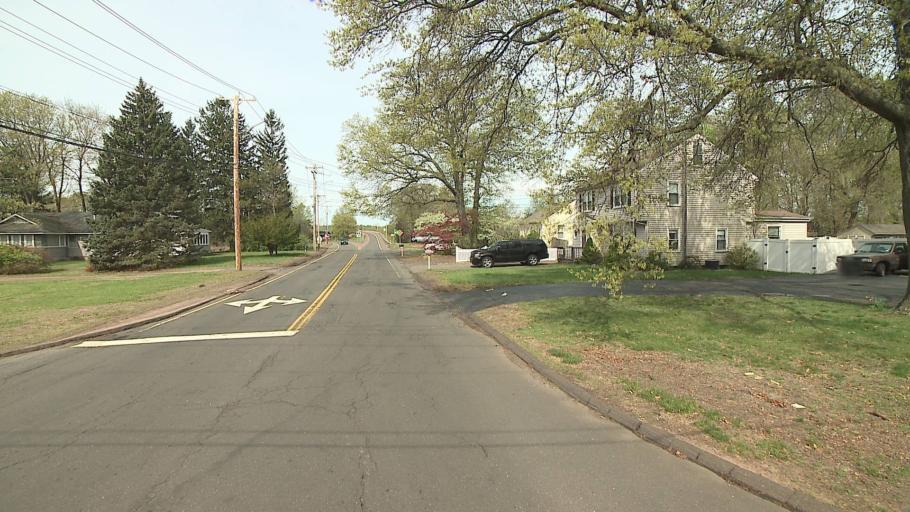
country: US
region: Connecticut
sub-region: New Haven County
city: North Haven
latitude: 41.3770
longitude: -72.8646
